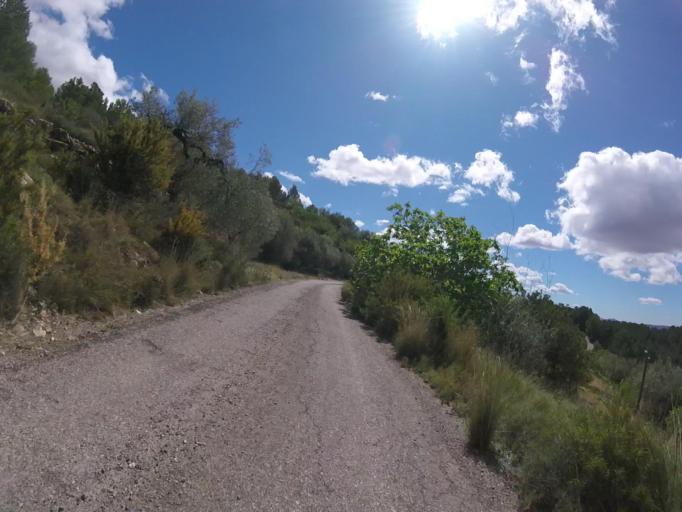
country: ES
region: Valencia
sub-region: Provincia de Castello
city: Sierra-Engarceran
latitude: 40.2696
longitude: -0.1018
